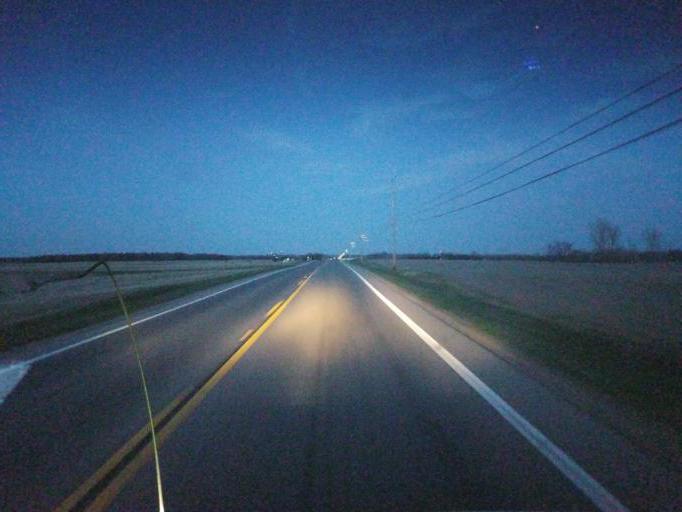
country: US
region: Ohio
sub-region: Logan County
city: Bellefontaine
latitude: 40.3653
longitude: -83.8280
